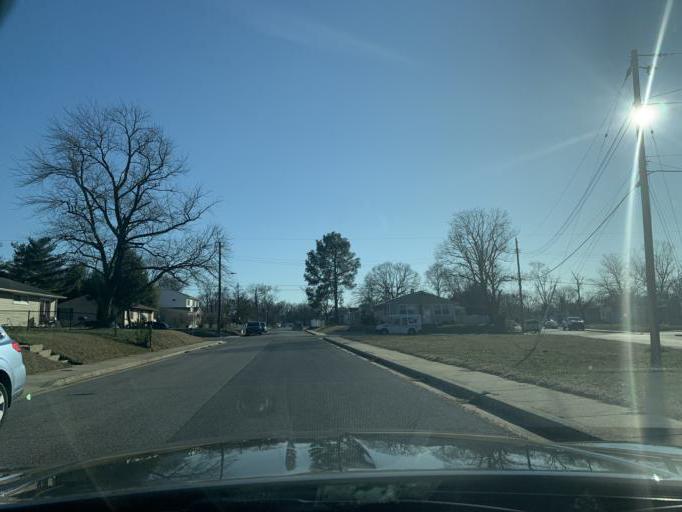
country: US
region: Maryland
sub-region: Anne Arundel County
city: Glen Burnie
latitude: 39.1555
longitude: -76.6253
